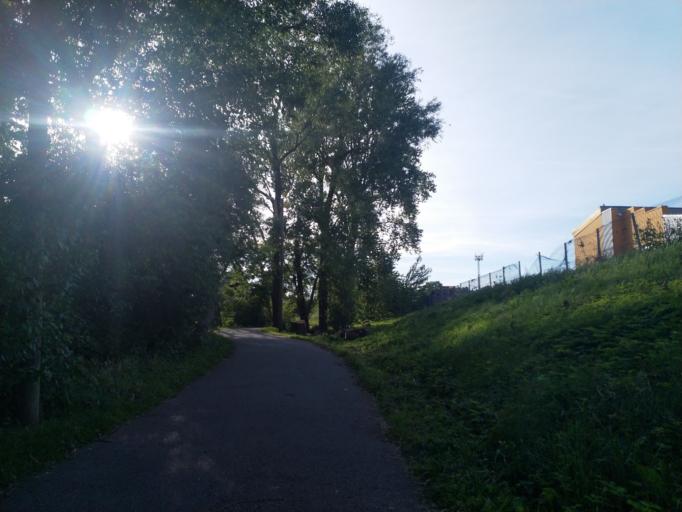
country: EE
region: Paernumaa
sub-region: Paernu linn
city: Parnu
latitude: 58.3874
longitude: 24.5284
